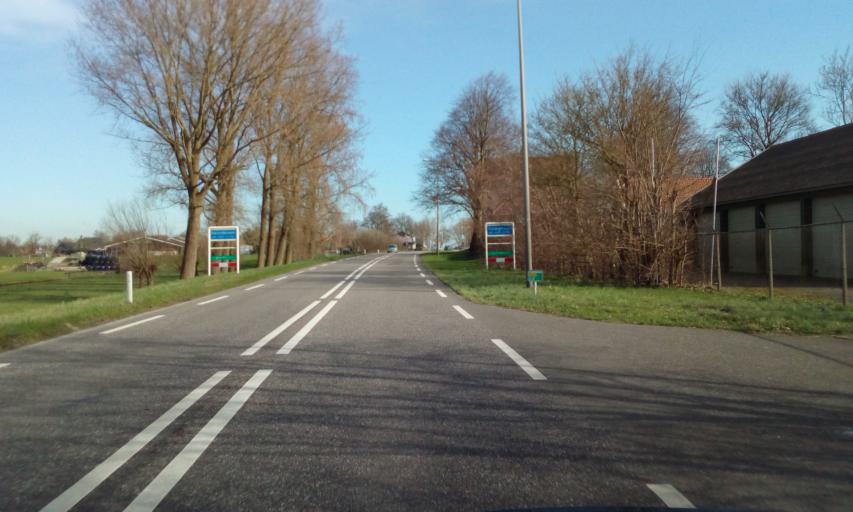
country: NL
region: South Holland
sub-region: Gemeente Nieuwkoop
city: Nieuwkoop
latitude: 52.1396
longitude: 4.7253
